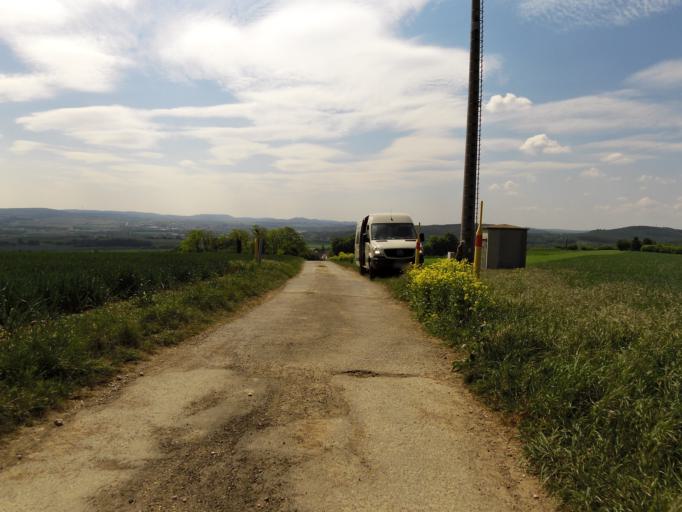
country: DE
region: Rheinland-Pfalz
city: Kerzenheim
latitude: 49.5820
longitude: 8.0603
